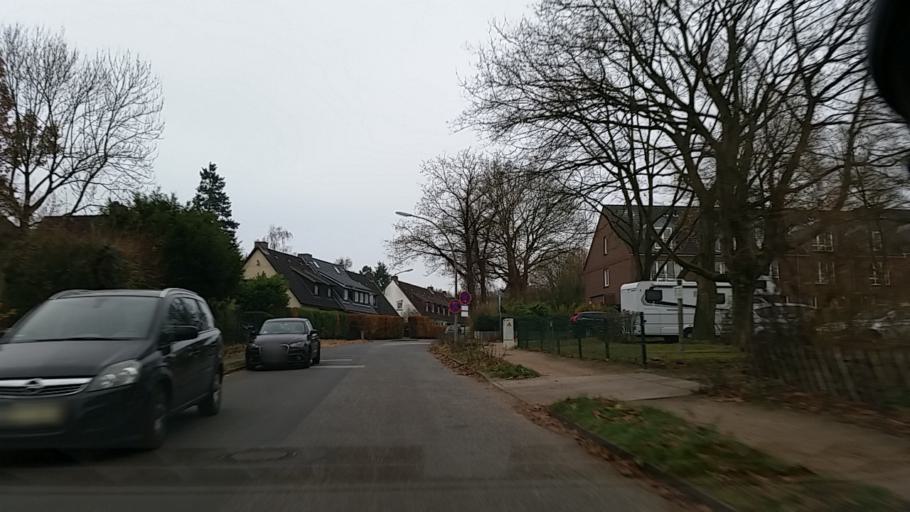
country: DE
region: Schleswig-Holstein
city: Rellingen
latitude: 53.5790
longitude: 9.7934
